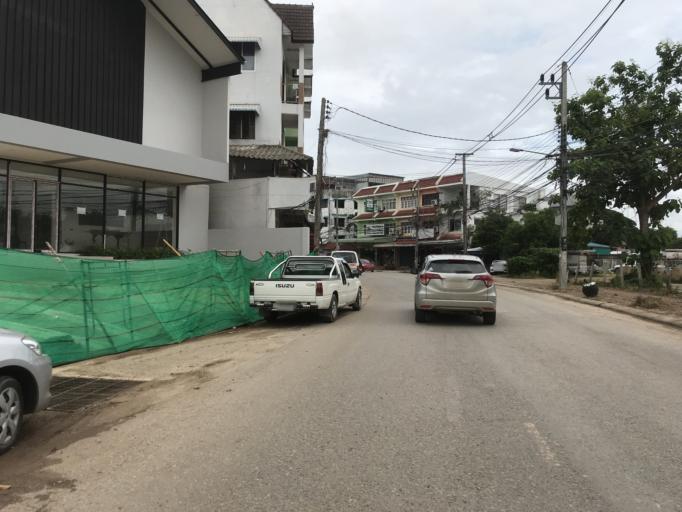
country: TH
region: Chiang Rai
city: Chiang Rai
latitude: 19.8980
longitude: 99.8308
